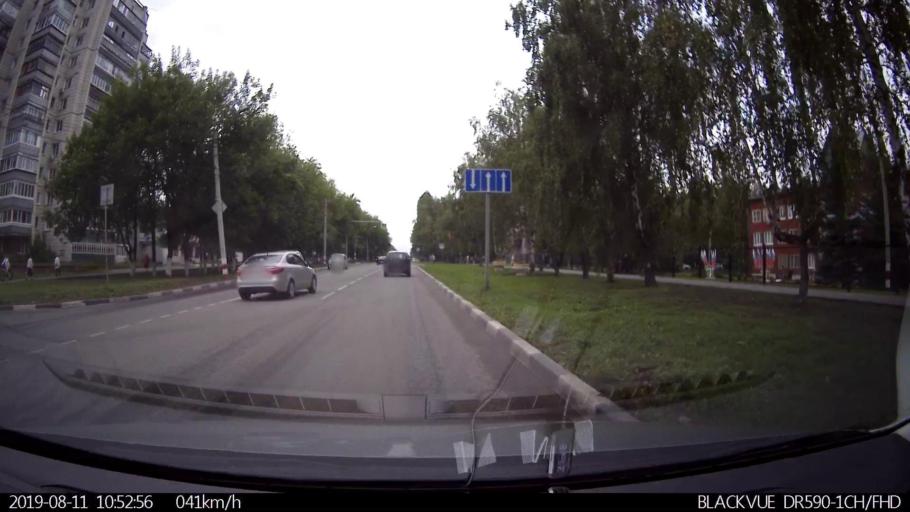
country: RU
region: Ulyanovsk
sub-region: Ulyanovskiy Rayon
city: Ulyanovsk
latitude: 54.2622
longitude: 48.3343
